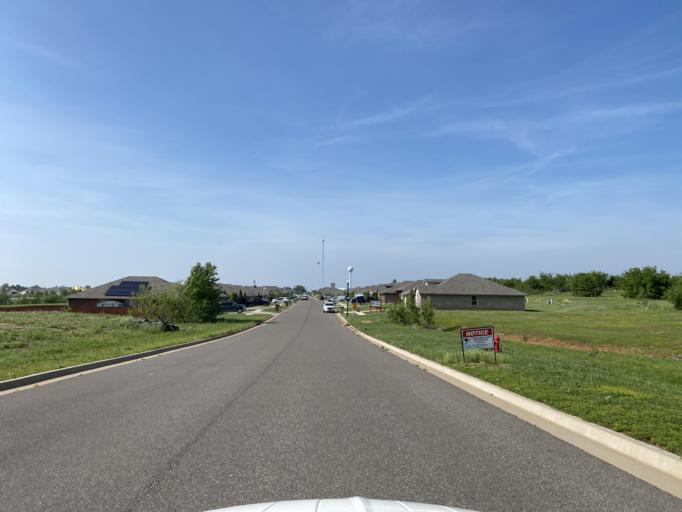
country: US
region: Oklahoma
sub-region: Oklahoma County
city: Midwest City
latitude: 35.4355
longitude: -97.3409
